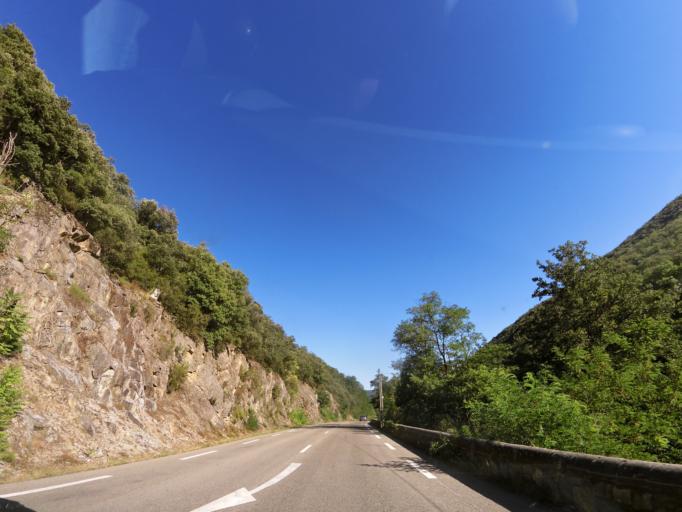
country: FR
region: Languedoc-Roussillon
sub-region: Departement du Gard
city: Valleraugue
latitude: 44.0716
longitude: 3.6741
